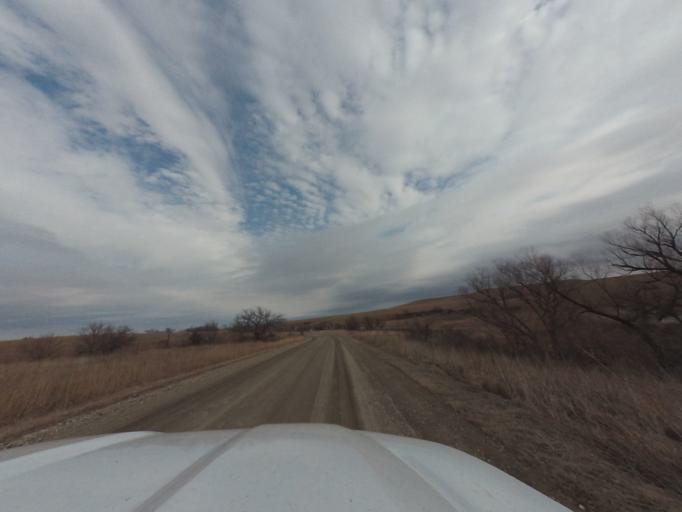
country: US
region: Kansas
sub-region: Chase County
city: Cottonwood Falls
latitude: 38.2521
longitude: -96.7298
